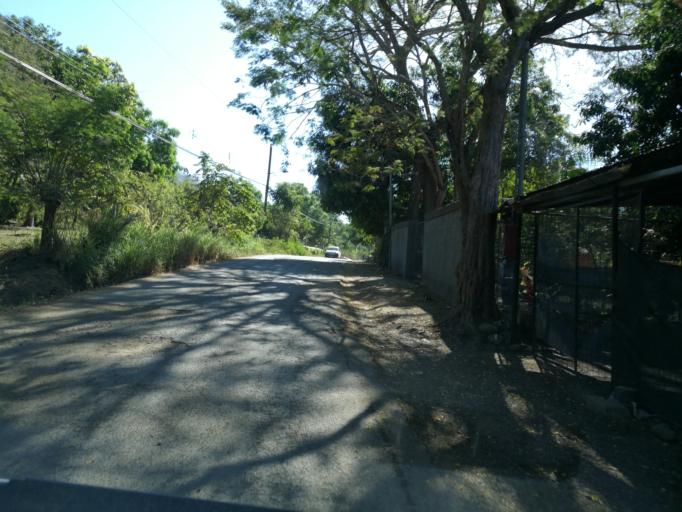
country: CR
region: Guanacaste
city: Juntas
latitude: 10.0994
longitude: -84.9920
